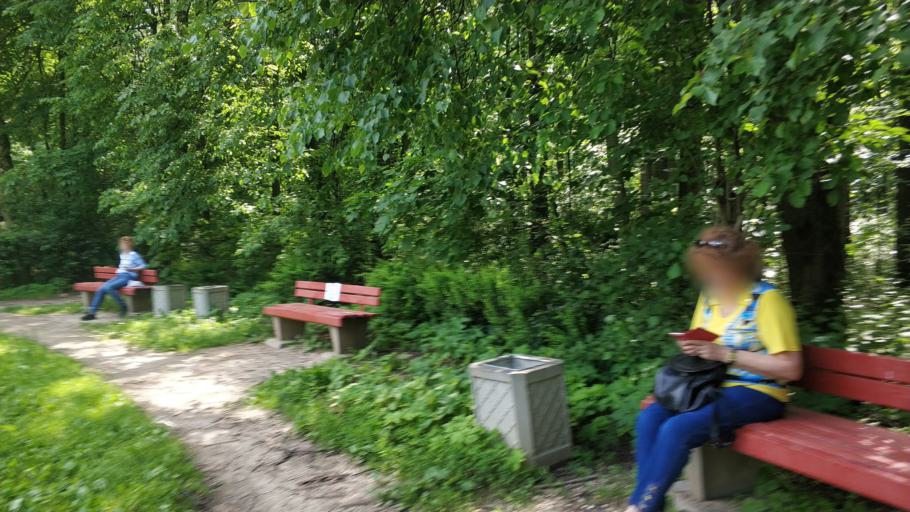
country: RU
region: Moscow
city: Perovo
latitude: 55.7314
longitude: 37.7992
